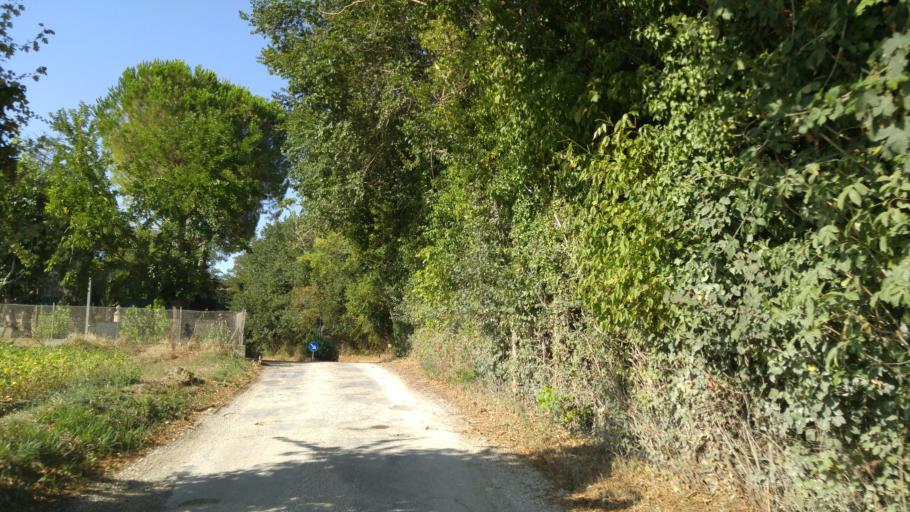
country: IT
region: The Marches
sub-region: Provincia di Pesaro e Urbino
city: Fenile
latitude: 43.8316
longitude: 12.9133
